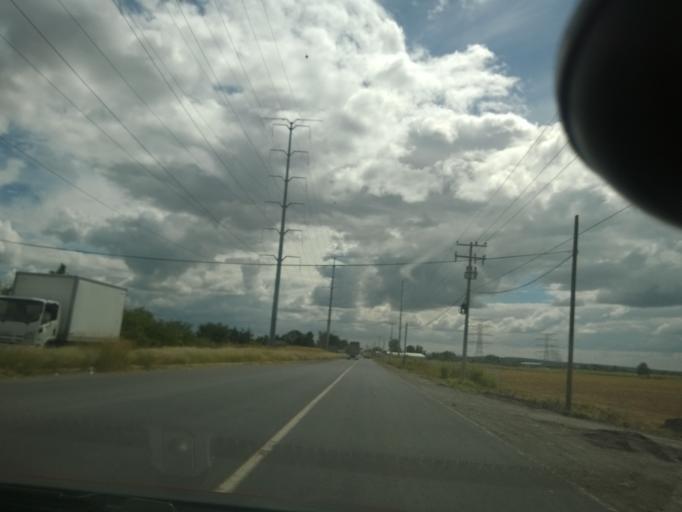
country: MX
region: Guanajuato
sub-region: Leon
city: El CERESO
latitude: 21.0291
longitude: -101.6960
